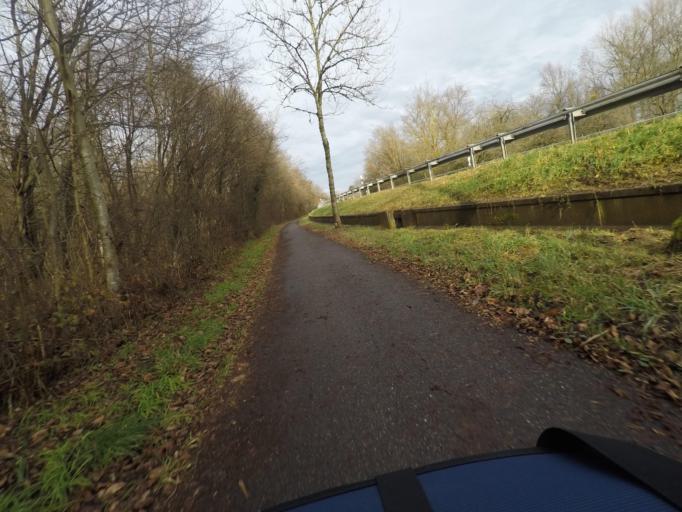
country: DE
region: Baden-Wuerttemberg
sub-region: Karlsruhe Region
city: Steinmauern
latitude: 48.9242
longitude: 8.2039
